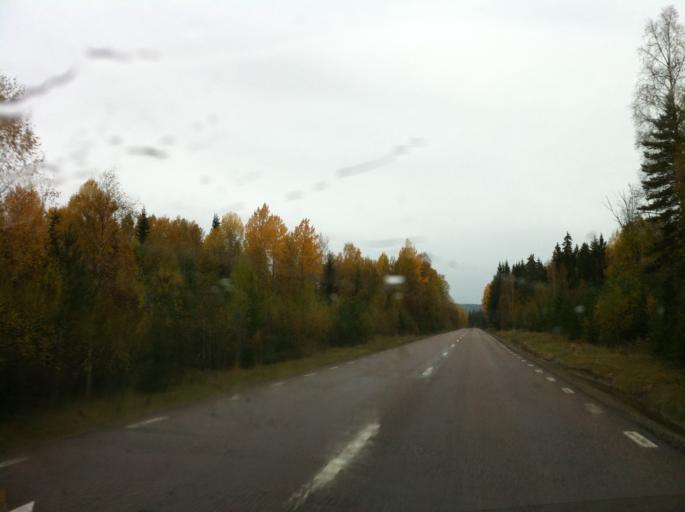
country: SE
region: Dalarna
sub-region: Ludvika Kommun
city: Grangesberg
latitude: 60.2347
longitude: 14.9888
